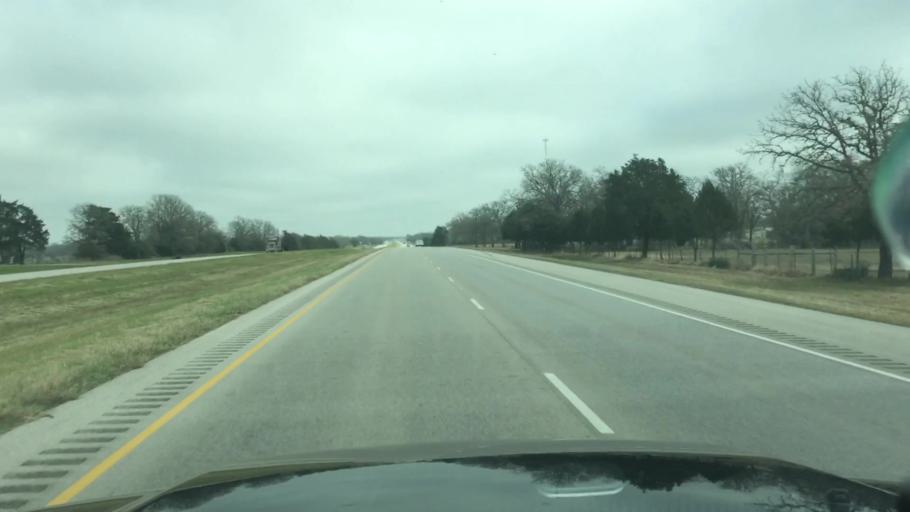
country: US
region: Texas
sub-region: Lee County
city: Giddings
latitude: 30.1463
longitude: -96.7129
